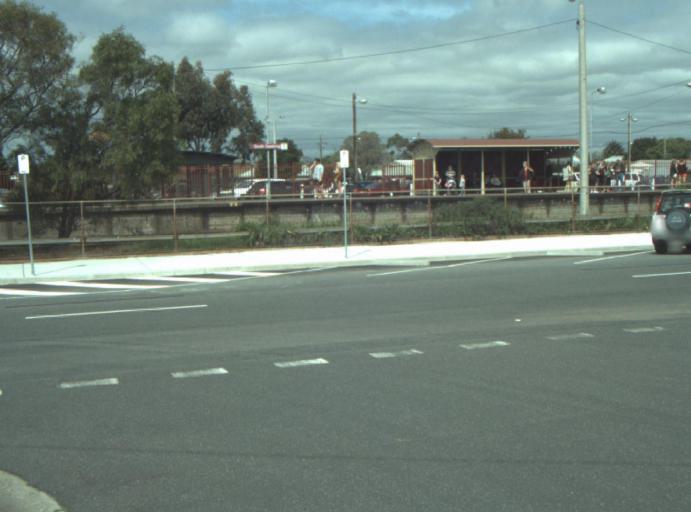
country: AU
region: Victoria
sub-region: Greater Geelong
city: Geelong
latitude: -38.1588
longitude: 144.3602
